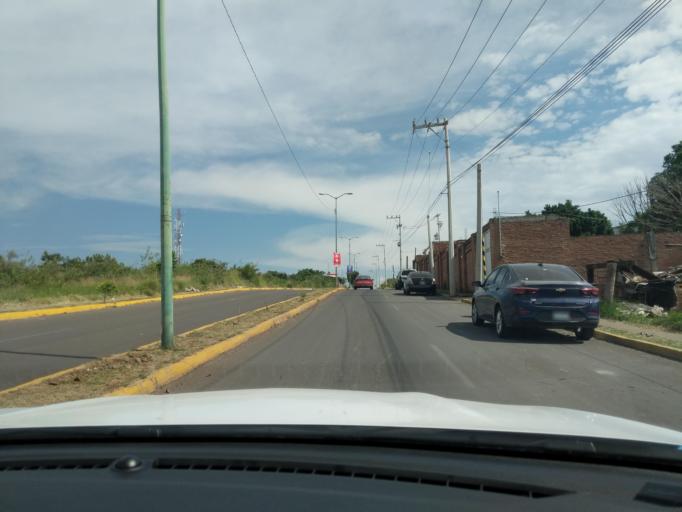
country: MX
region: Jalisco
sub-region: El Salto
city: Hacienda Vieja del Castillo (Castillo Viejo)
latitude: 20.5282
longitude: -103.2366
